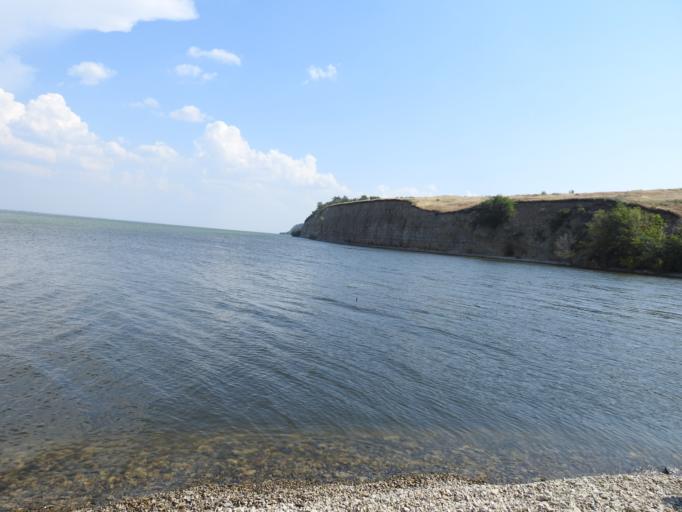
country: RU
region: Saratov
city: Rovnoye
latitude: 50.4927
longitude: 45.8006
